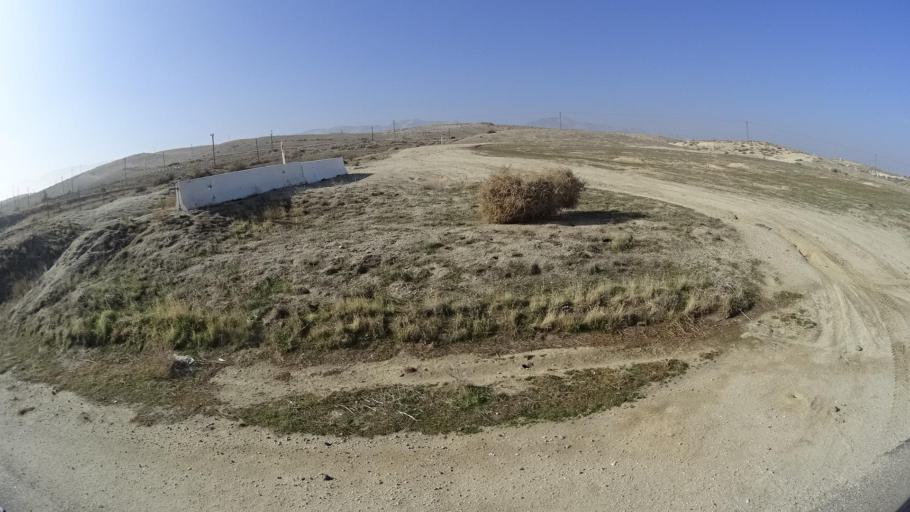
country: US
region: California
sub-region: Kern County
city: Taft Heights
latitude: 35.1696
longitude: -119.5339
